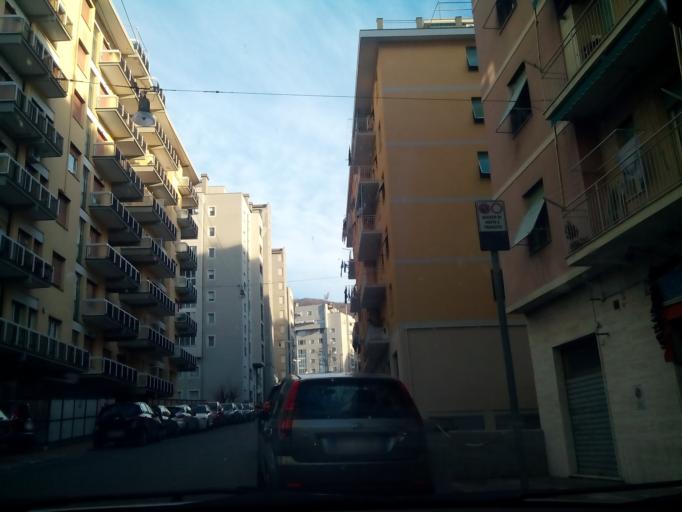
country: IT
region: Liguria
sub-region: Provincia di Genova
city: Piccarello
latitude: 44.4549
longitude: 8.9810
